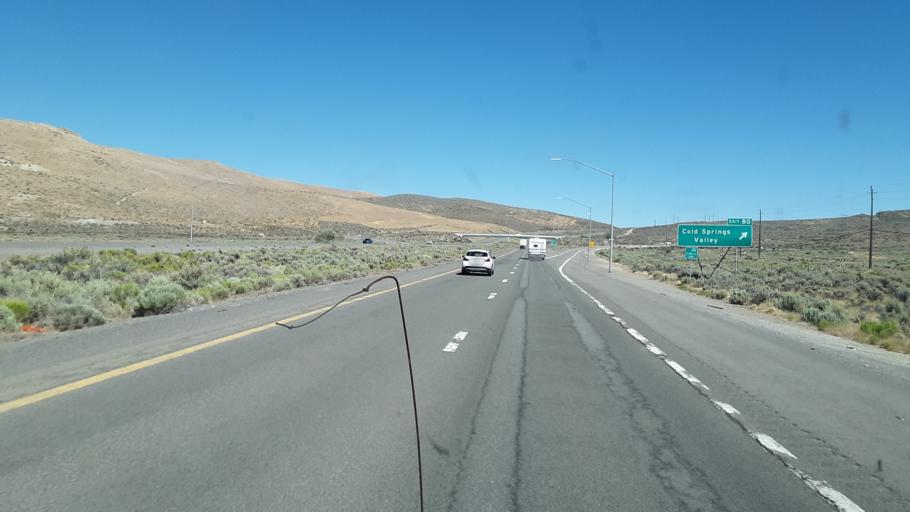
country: US
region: Nevada
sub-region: Washoe County
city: Cold Springs
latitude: 39.6461
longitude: -119.9651
